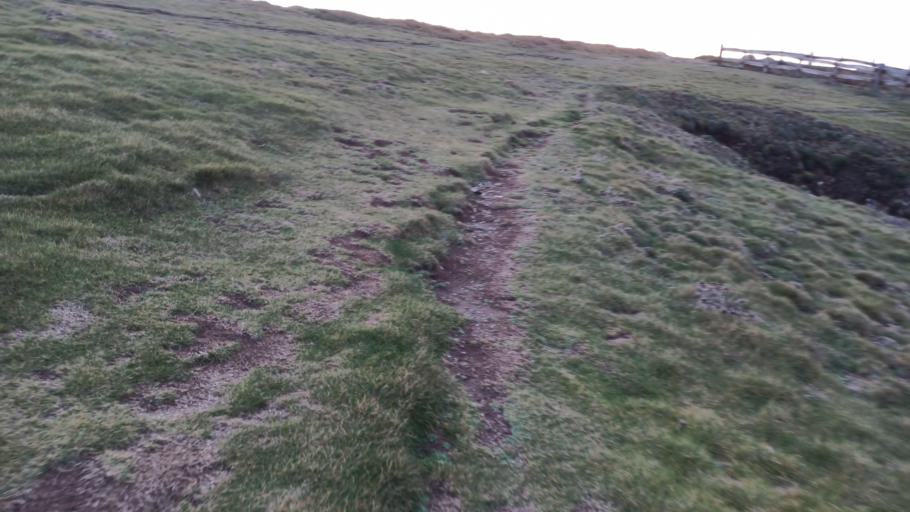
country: ES
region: Galicia
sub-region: Provincia da Coruna
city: A Coruna
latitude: 43.3963
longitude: -8.3467
